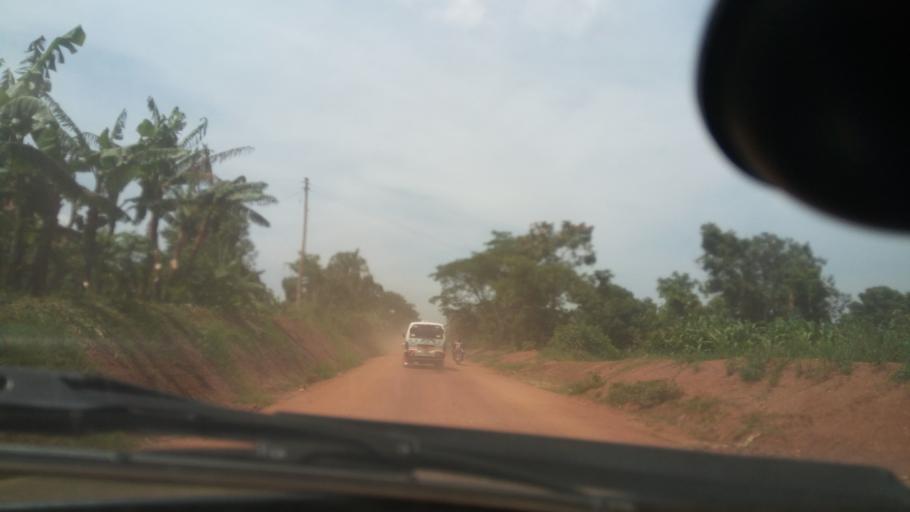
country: UG
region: Central Region
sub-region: Mityana District
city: Mityana
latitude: 0.4985
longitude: 32.1319
